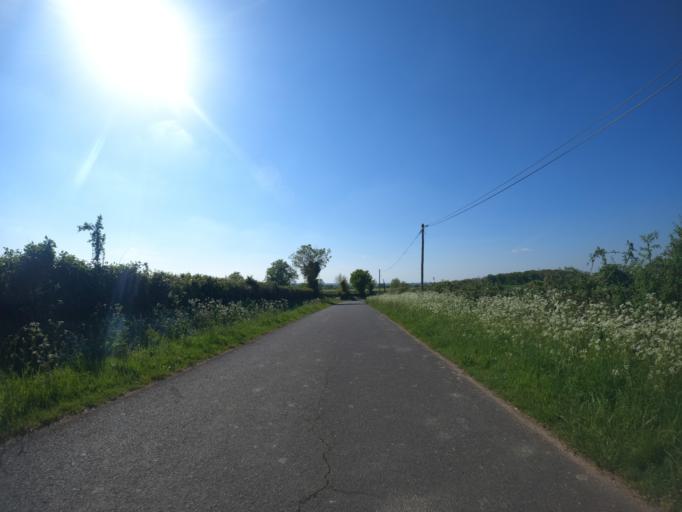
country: FR
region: Poitou-Charentes
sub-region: Departement des Deux-Sevres
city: Moncoutant
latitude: 46.6835
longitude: -0.5298
